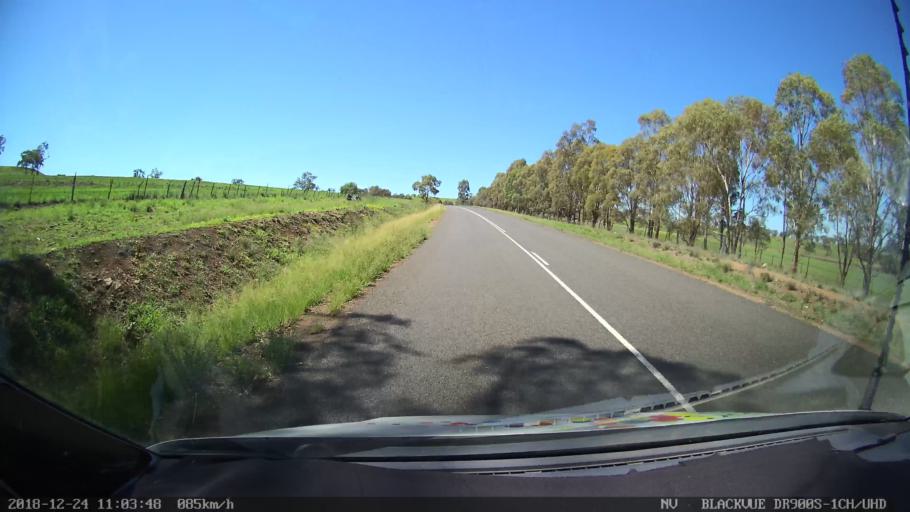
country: AU
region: New South Wales
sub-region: Upper Hunter Shire
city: Merriwa
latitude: -32.1014
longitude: 150.3689
